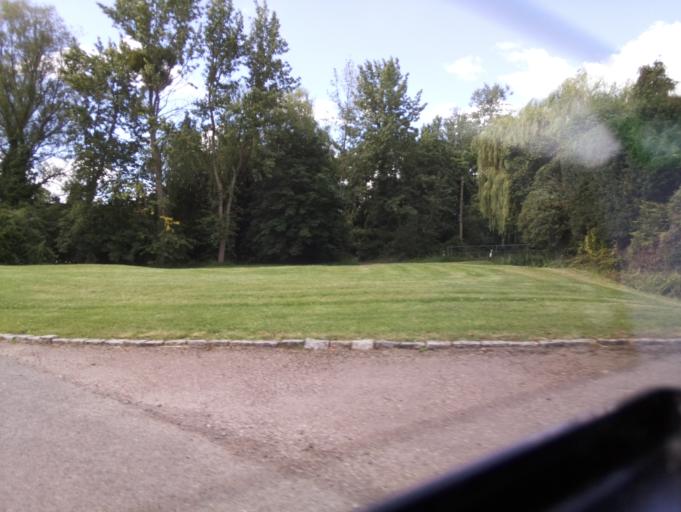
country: GB
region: England
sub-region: Gloucestershire
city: Newent
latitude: 51.8435
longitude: -2.3625
